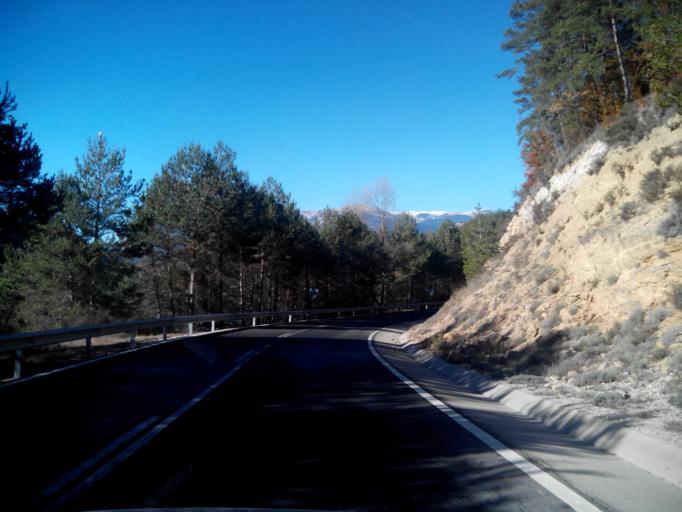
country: ES
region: Catalonia
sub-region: Provincia de Barcelona
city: Capolat
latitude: 42.1190
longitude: 1.6884
